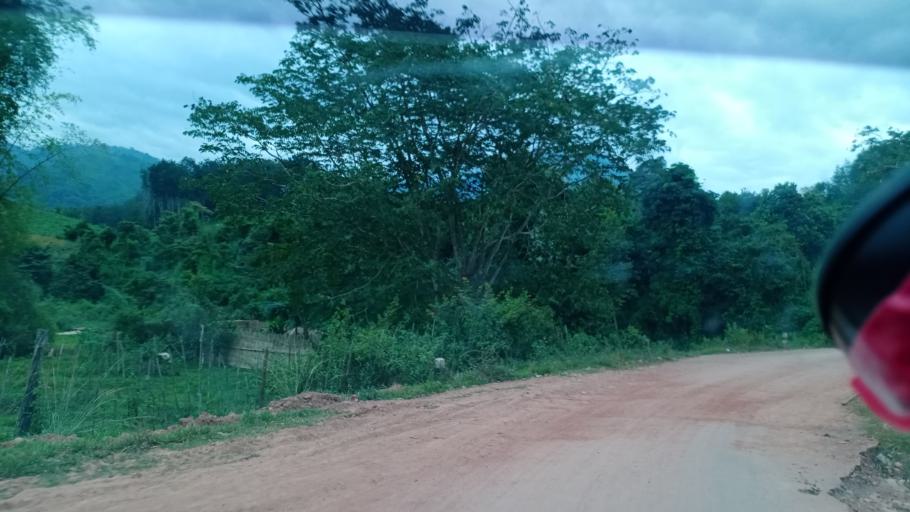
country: TH
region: Changwat Bueng Kan
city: Pak Khat
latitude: 18.7152
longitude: 103.2110
